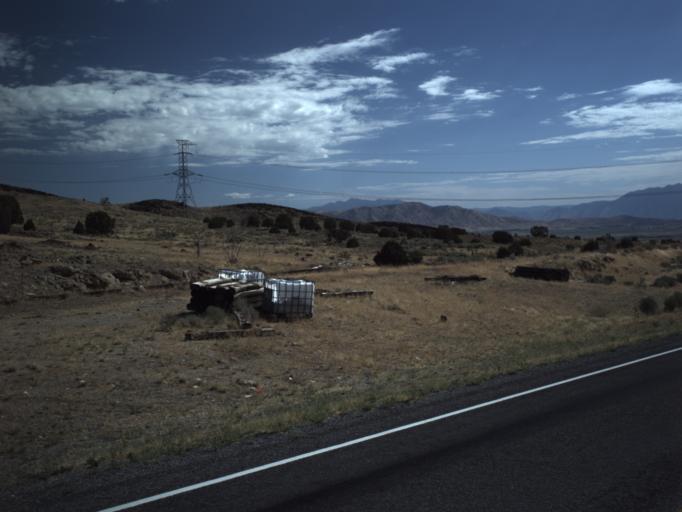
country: US
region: Utah
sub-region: Utah County
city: Genola
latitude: 39.9503
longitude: -112.0169
